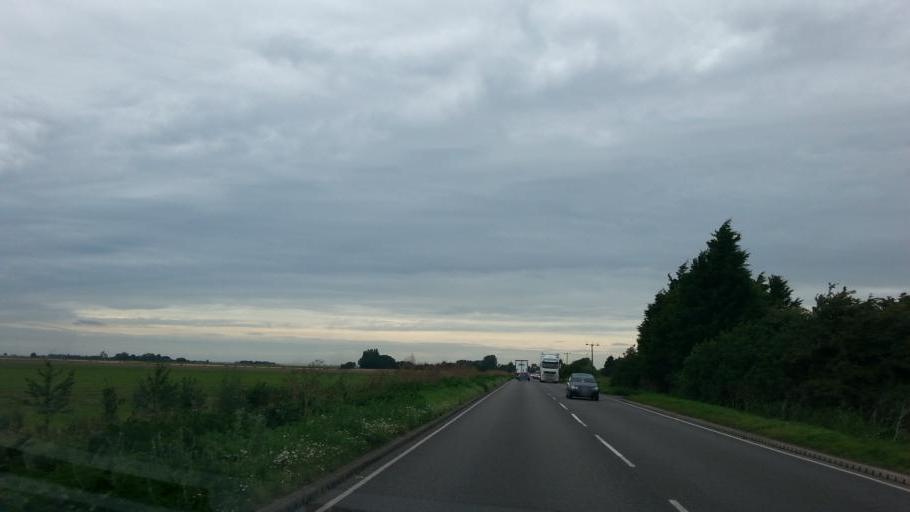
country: GB
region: England
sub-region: Cambridgeshire
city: March
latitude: 52.6109
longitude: 0.0291
